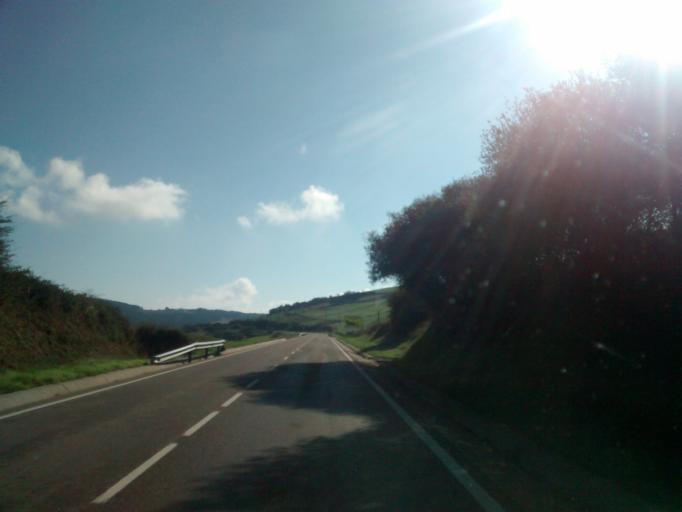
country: ES
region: Cantabria
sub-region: Provincia de Cantabria
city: Reinosa
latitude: 42.9903
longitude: -4.1162
